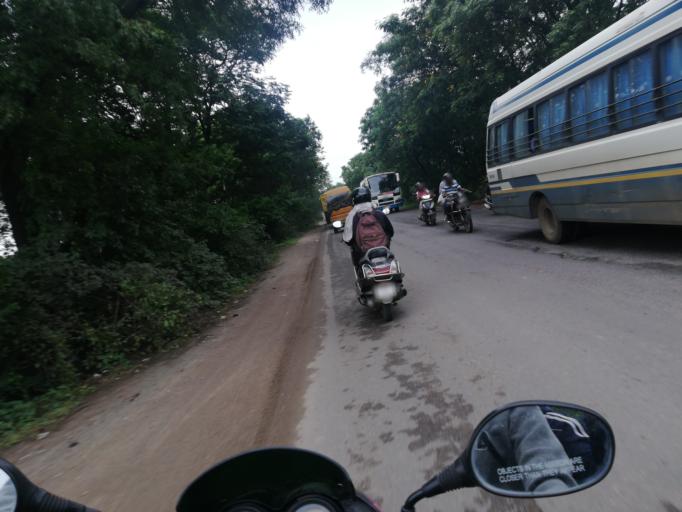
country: IN
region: Telangana
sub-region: Rangareddi
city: Kukatpalli
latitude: 17.5586
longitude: 78.4115
